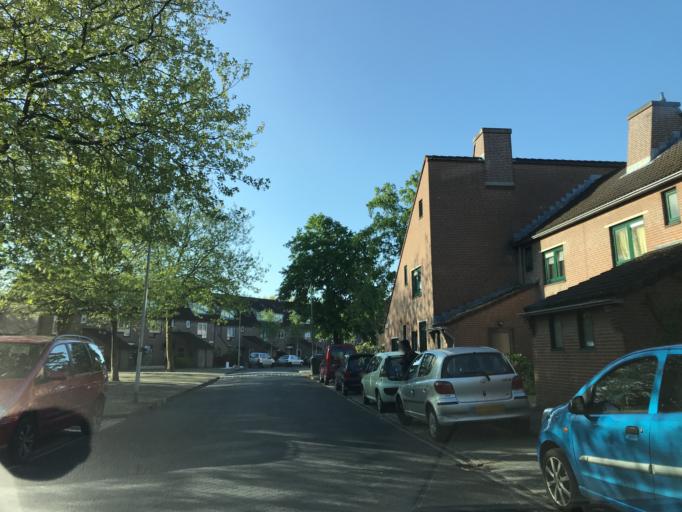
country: NL
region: North Holland
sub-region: Gemeente Diemen
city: Diemen
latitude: 52.3358
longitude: 4.9617
